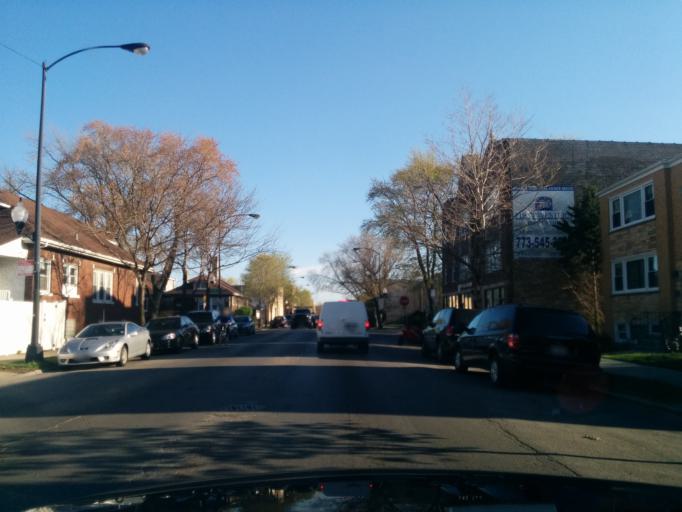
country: US
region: Illinois
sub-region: Cook County
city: Elmwood Park
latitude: 41.9338
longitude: -87.7565
